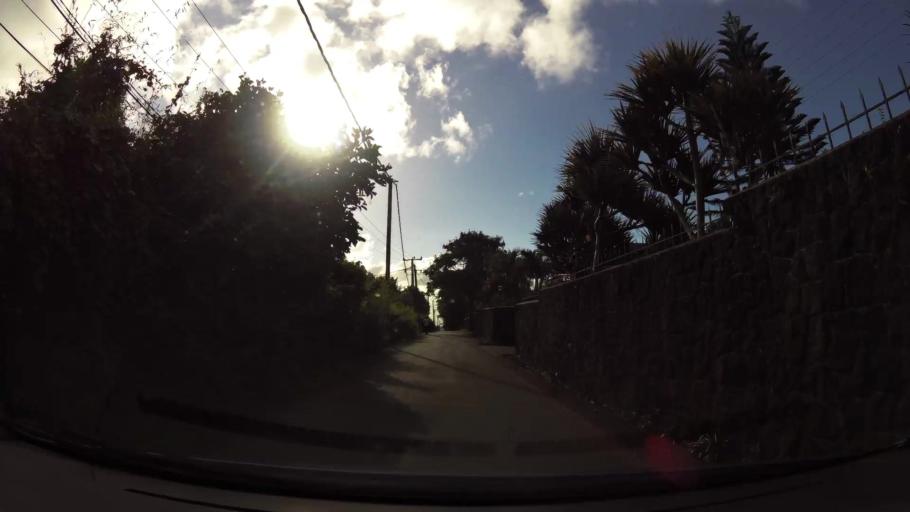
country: MU
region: Plaines Wilhems
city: Curepipe
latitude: -20.3177
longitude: 57.5006
